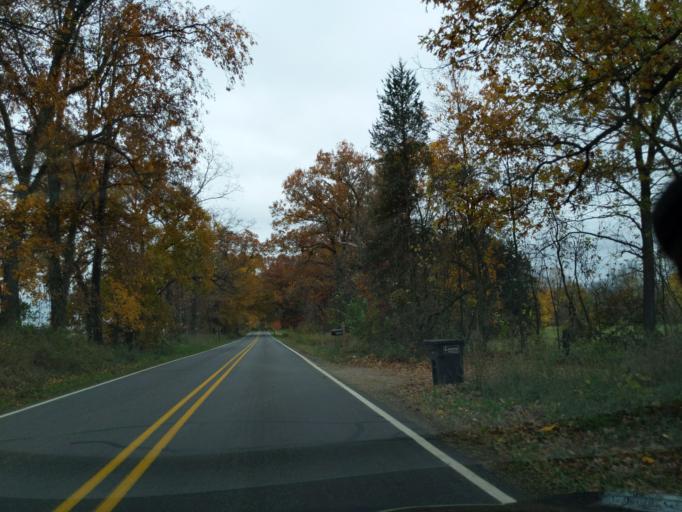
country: US
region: Michigan
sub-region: Jackson County
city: Spring Arbor
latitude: 42.3267
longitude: -84.6005
